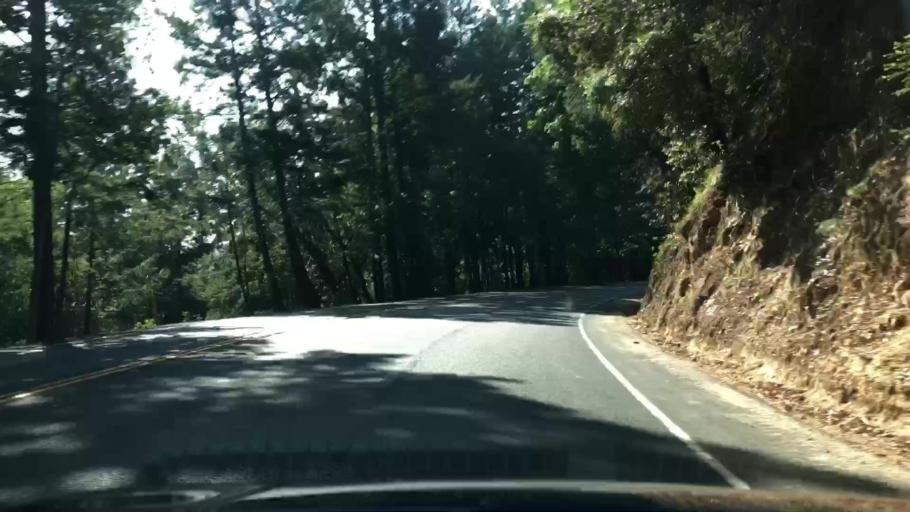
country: US
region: California
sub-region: Napa County
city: Calistoga
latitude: 38.6607
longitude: -122.5958
